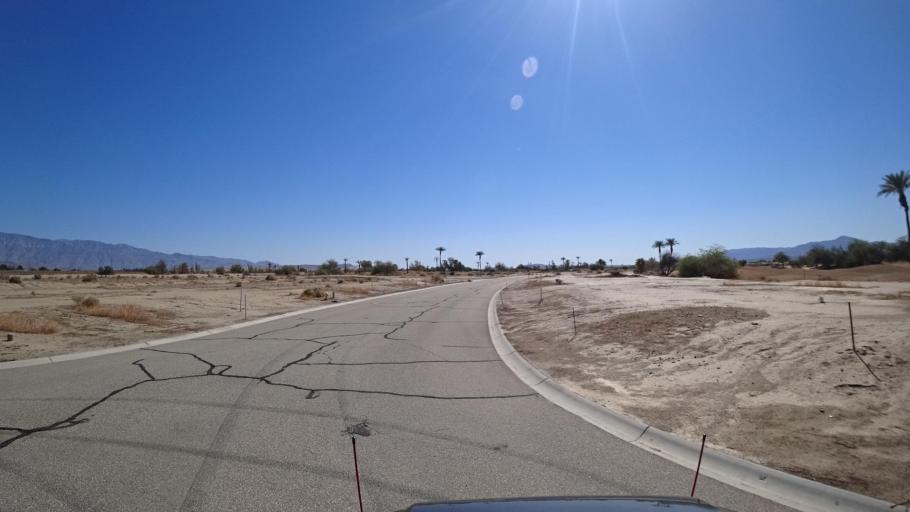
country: US
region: California
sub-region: San Diego County
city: Borrego Springs
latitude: 33.2475
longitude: -116.3566
